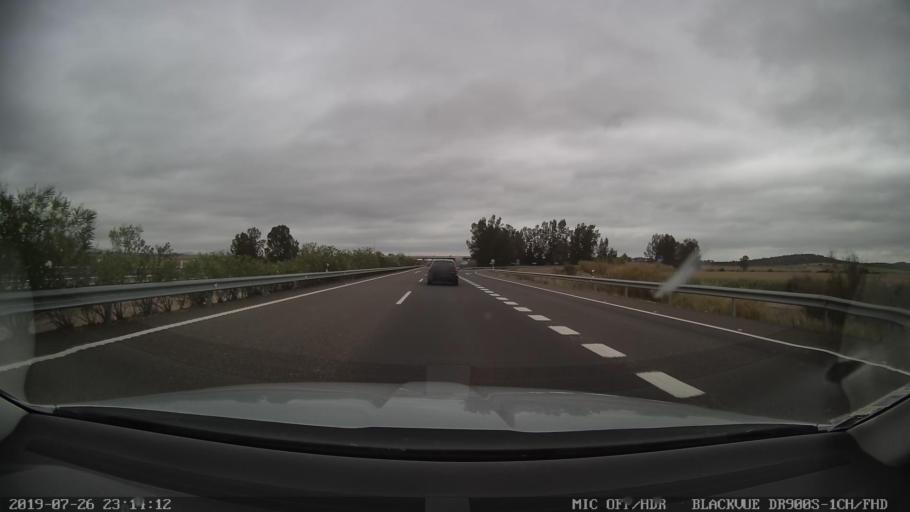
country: ES
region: Extremadura
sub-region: Provincia de Badajoz
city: Santa Amalia
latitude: 39.0334
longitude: -6.0696
